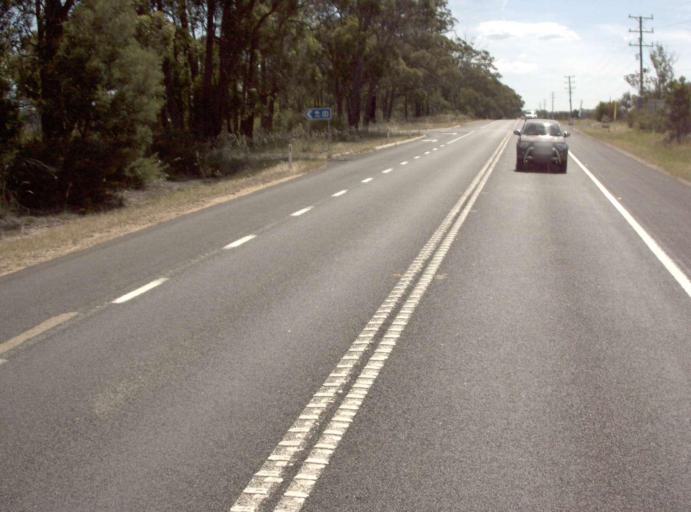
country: AU
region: Victoria
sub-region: Wellington
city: Sale
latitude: -37.9207
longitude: 147.2729
